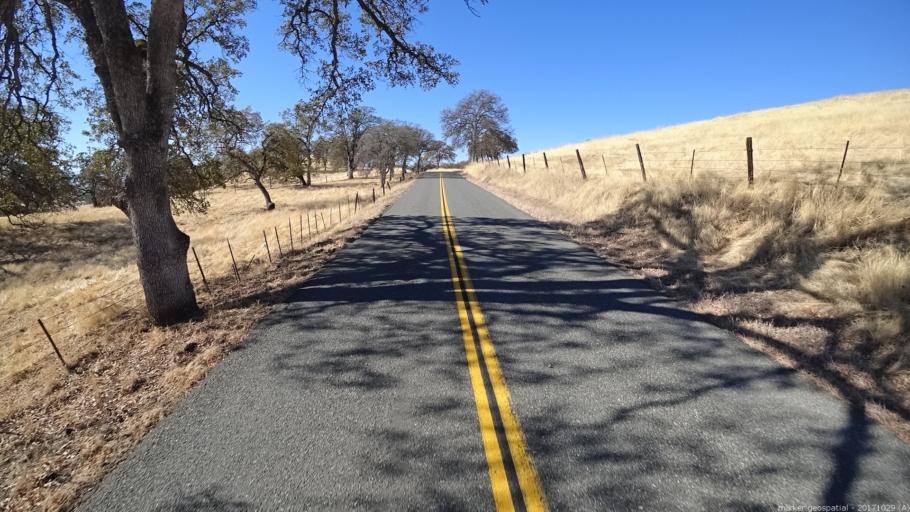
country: US
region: California
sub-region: Shasta County
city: Shasta
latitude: 40.4469
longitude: -122.6490
